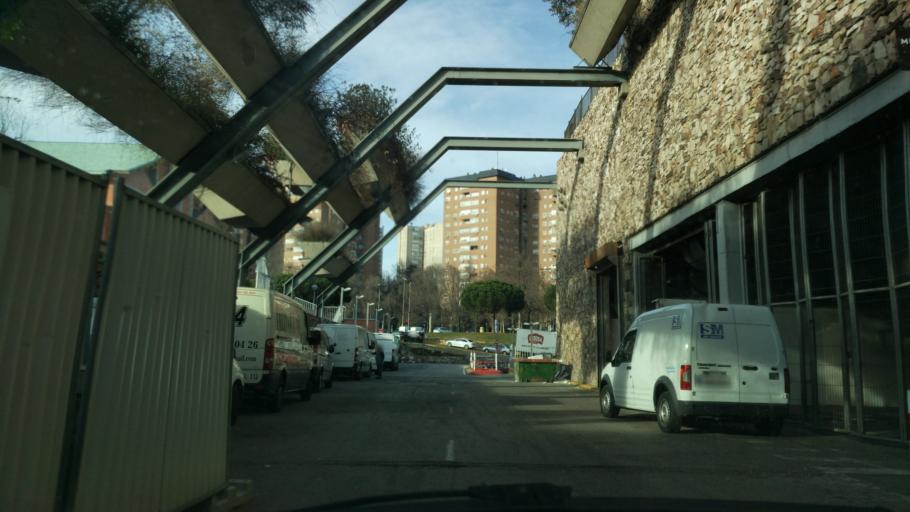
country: ES
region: Madrid
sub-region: Provincia de Madrid
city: Tetuan de las Victorias
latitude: 40.4795
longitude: -3.7087
